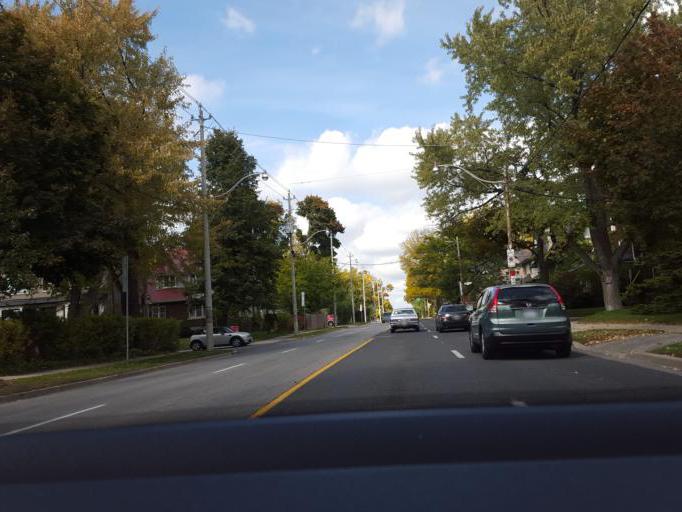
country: CA
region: Ontario
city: Toronto
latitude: 43.7226
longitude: -79.3958
